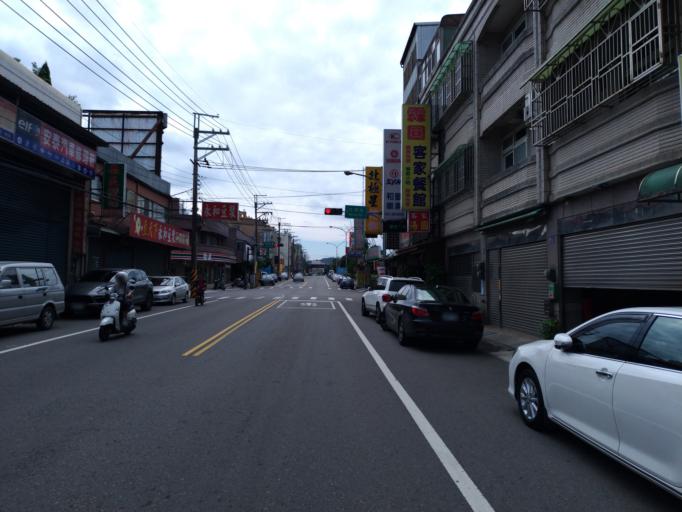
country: TW
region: Taiwan
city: Daxi
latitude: 24.9175
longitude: 121.1453
